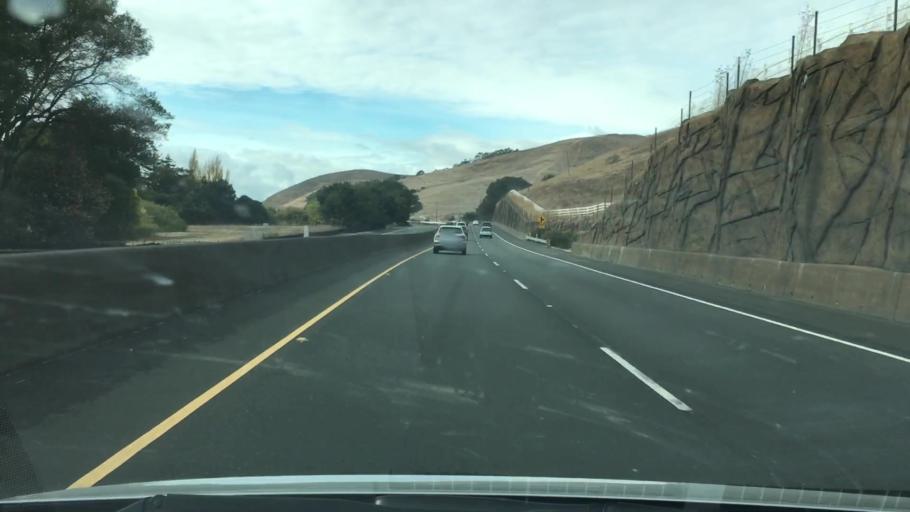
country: US
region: California
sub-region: Solano County
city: Green Valley
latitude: 38.2073
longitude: -122.1811
